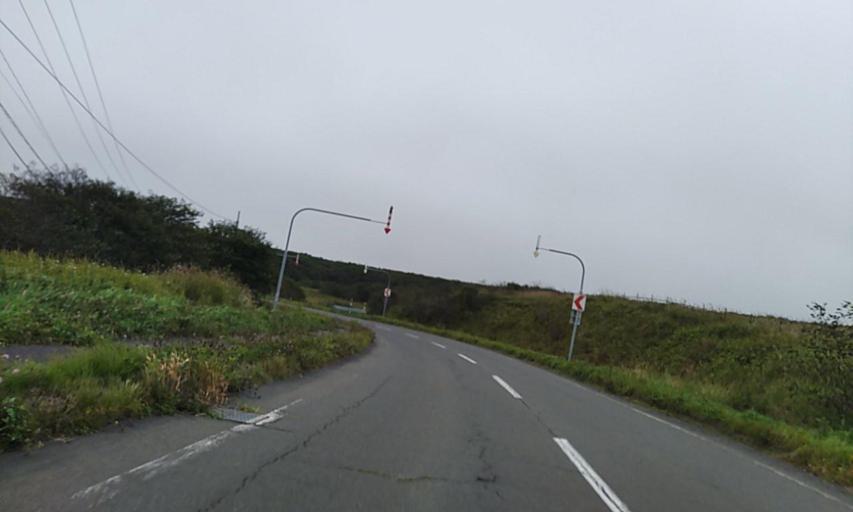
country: JP
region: Hokkaido
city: Nemuro
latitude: 43.3816
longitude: 145.6953
